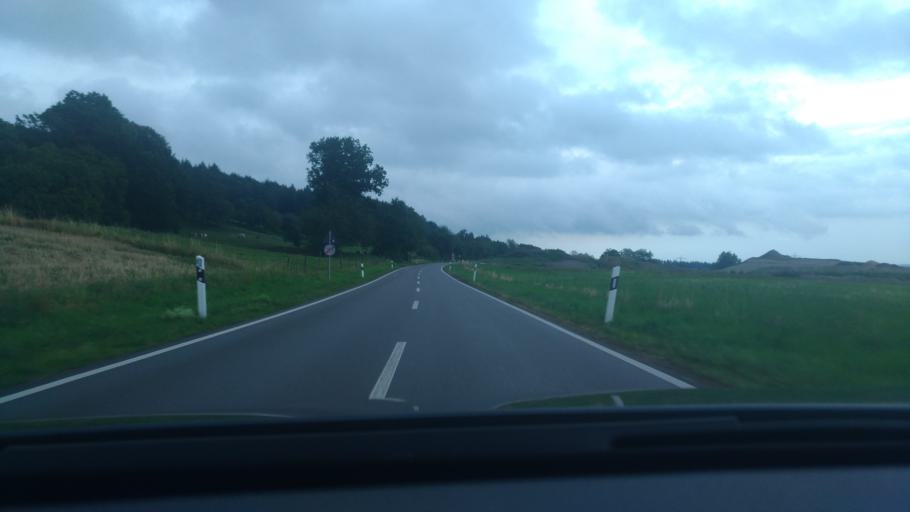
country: DE
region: Baden-Wuerttemberg
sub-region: Tuebingen Region
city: Owingen
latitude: 47.7989
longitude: 9.1389
